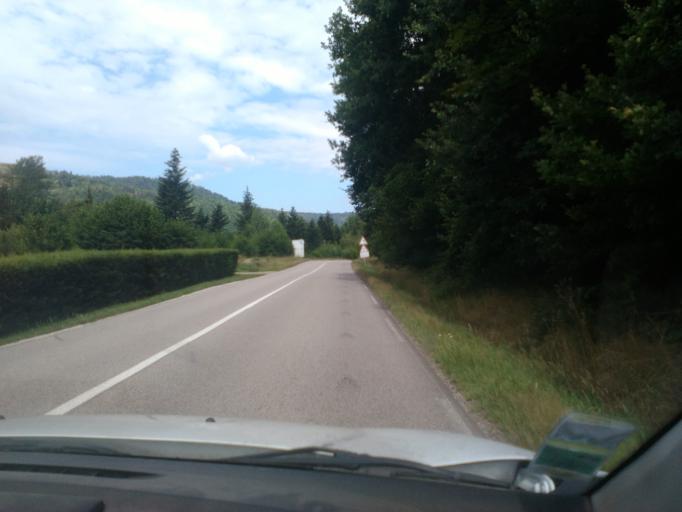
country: FR
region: Lorraine
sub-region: Departement des Vosges
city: Saulxures-sur-Moselotte
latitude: 47.9547
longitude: 6.7485
